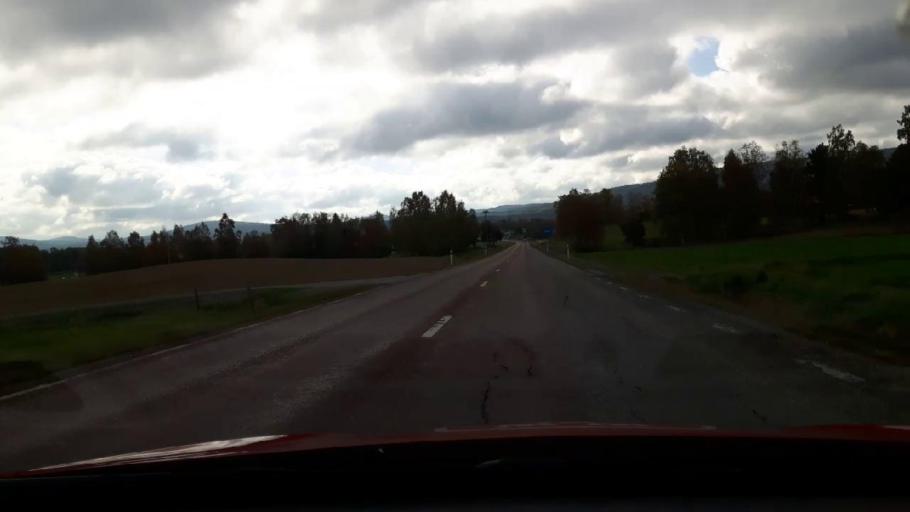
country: SE
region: Gaevleborg
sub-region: Ljusdals Kommun
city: Jaervsoe
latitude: 61.6792
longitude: 16.1453
